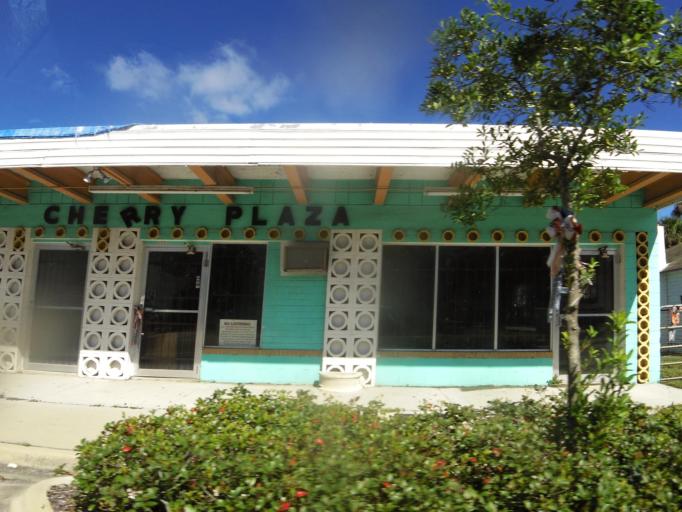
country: US
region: Florida
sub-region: Seminole County
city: Sanford
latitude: 28.8009
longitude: -81.2808
